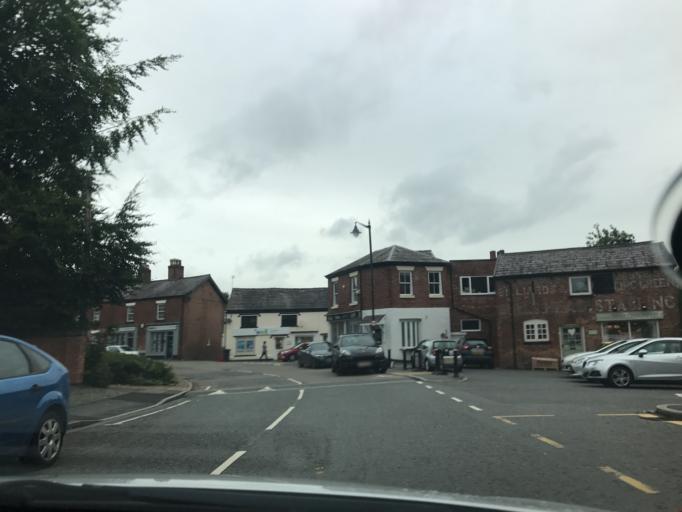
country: GB
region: England
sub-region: Cheshire West and Chester
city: Northwich
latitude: 53.2353
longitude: -2.5108
